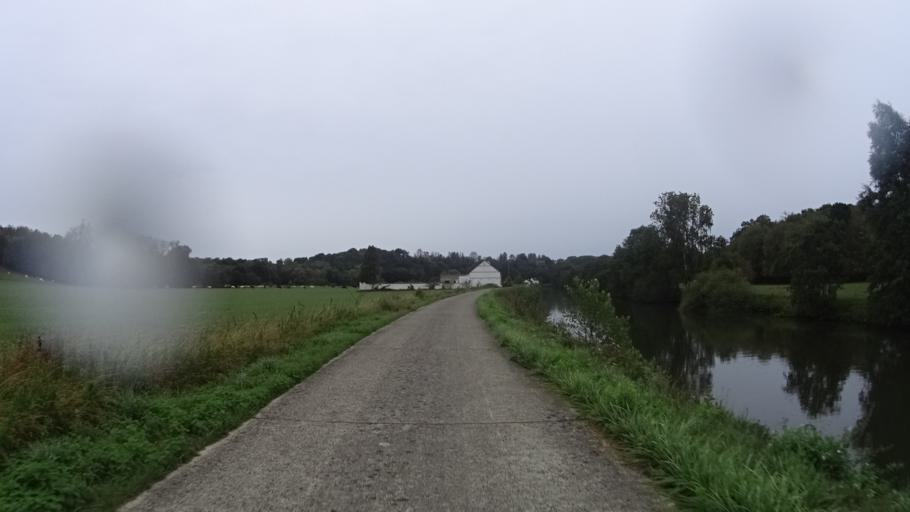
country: BE
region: Wallonia
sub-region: Province du Hainaut
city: Lobbes
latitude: 50.3272
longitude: 4.2301
